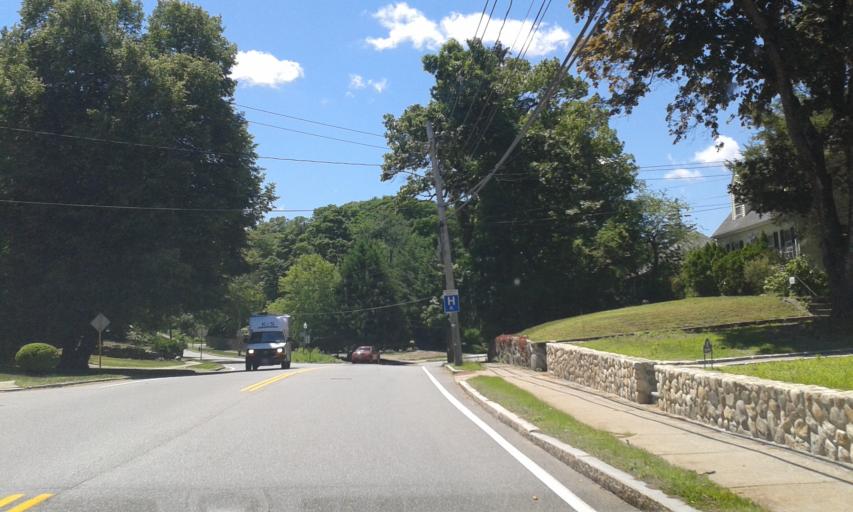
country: US
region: Massachusetts
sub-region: Middlesex County
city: Stoneham
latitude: 42.4693
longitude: -71.1200
